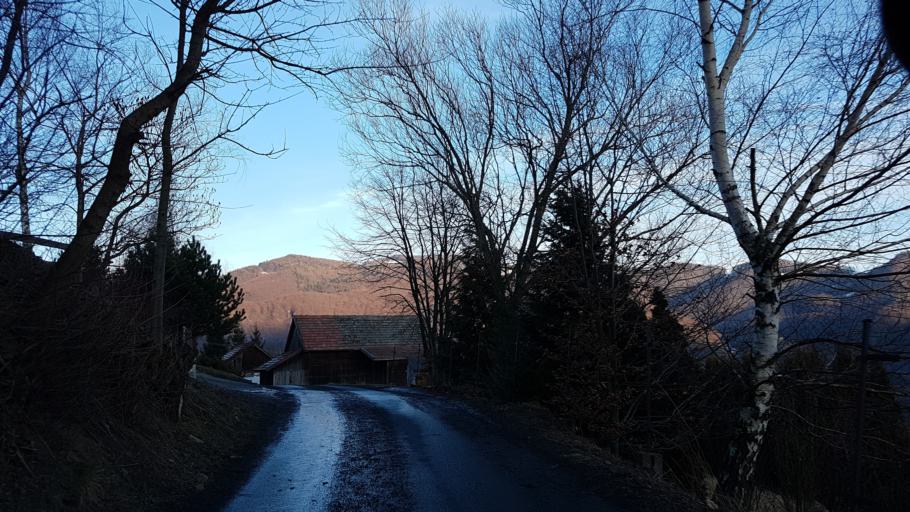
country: PL
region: Lesser Poland Voivodeship
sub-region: Powiat nowosadecki
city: Rytro
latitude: 49.4920
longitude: 20.6707
